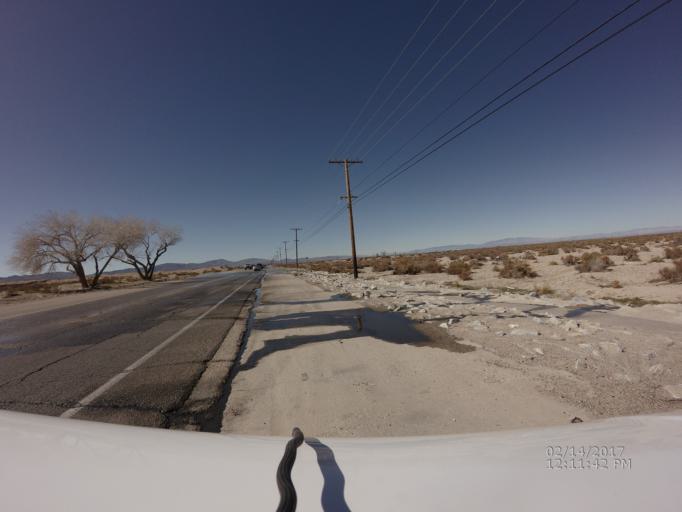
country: US
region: California
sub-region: Los Angeles County
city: Littlerock
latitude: 34.5798
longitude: -117.9760
